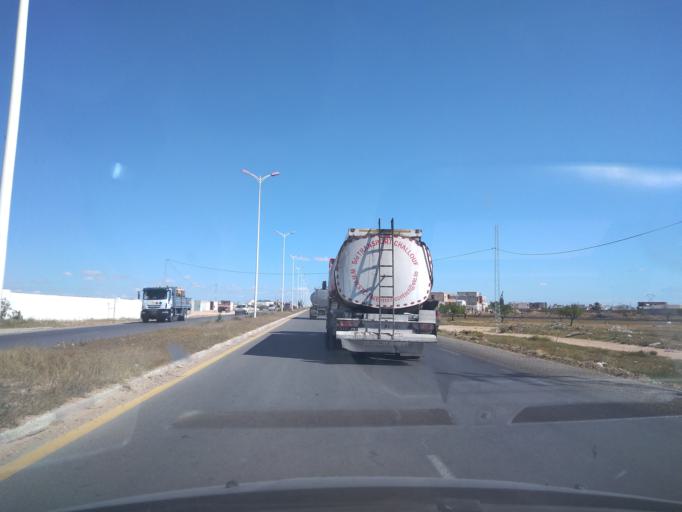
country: TN
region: Safaqis
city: Sfax
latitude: 34.8044
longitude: 10.6901
